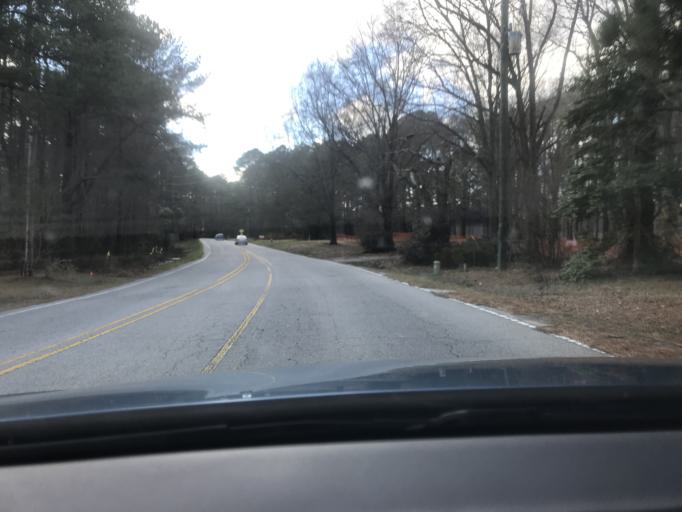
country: US
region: North Carolina
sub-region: Wake County
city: Apex
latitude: 35.7168
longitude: -78.7903
